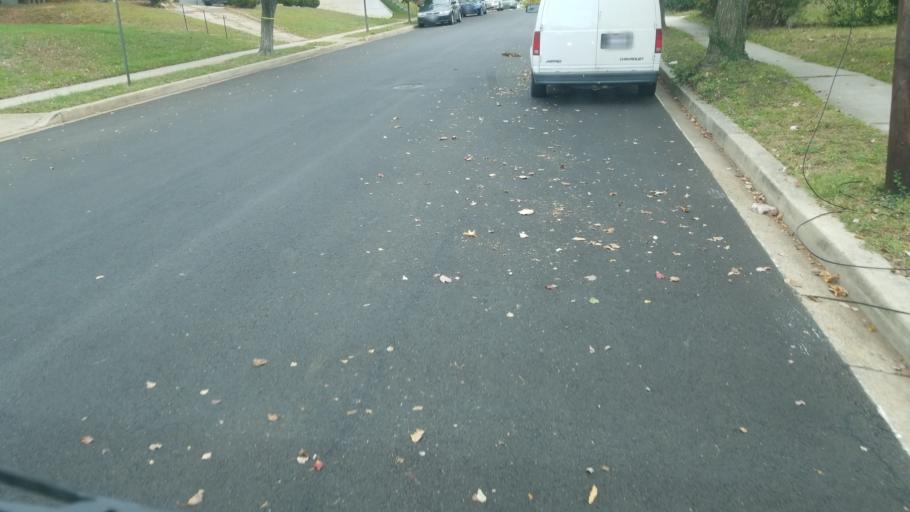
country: US
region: Maryland
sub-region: Prince George's County
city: Capitol Heights
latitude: 38.8908
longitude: -76.9294
